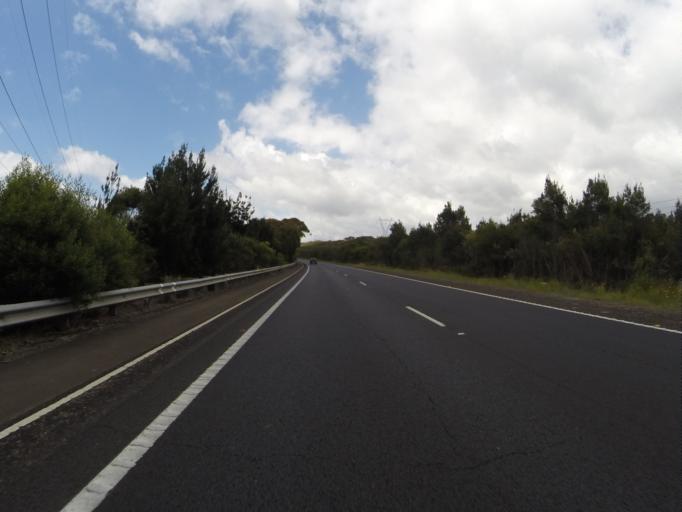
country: AU
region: New South Wales
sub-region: Wollongong
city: Helensburgh
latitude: -34.2248
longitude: 150.9505
